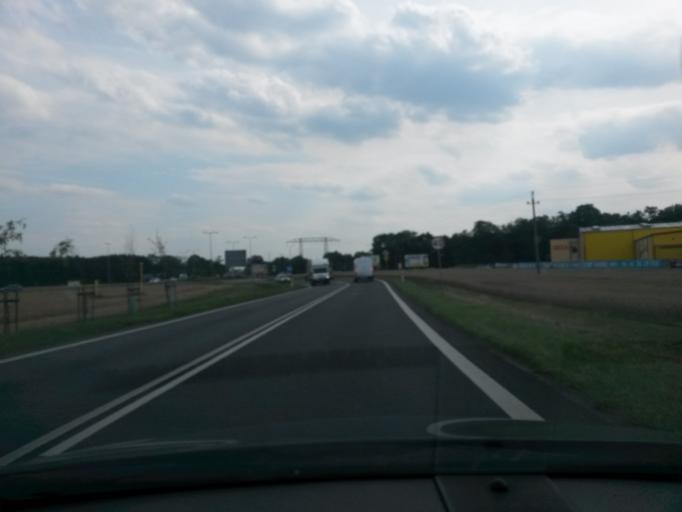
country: PL
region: Greater Poland Voivodeship
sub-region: Powiat sremski
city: Srem
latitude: 52.1079
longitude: 17.0432
